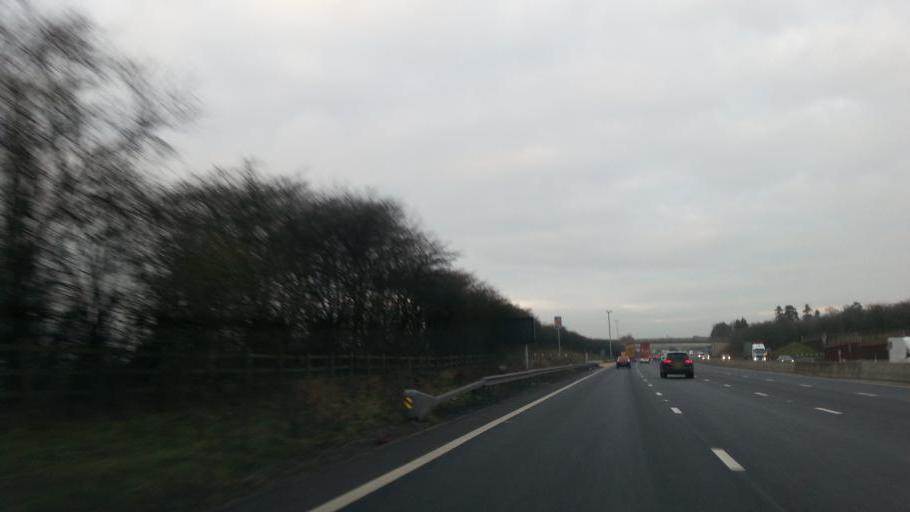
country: GB
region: England
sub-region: Worcestershire
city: Bromsgrove
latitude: 52.3177
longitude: -2.0975
